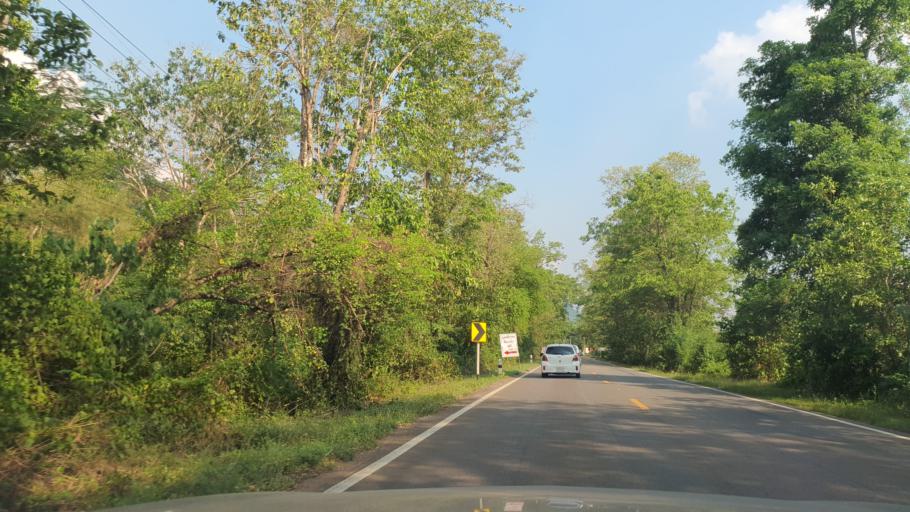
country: TH
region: Kanchanaburi
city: Sai Yok
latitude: 14.3235
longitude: 99.2052
